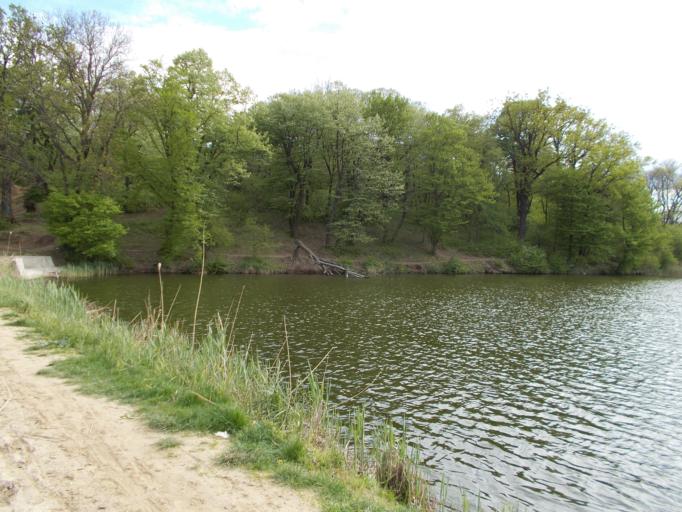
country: RO
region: Ilfov
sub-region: Comuna Branesti
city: Branesti
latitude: 44.4491
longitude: 26.3267
